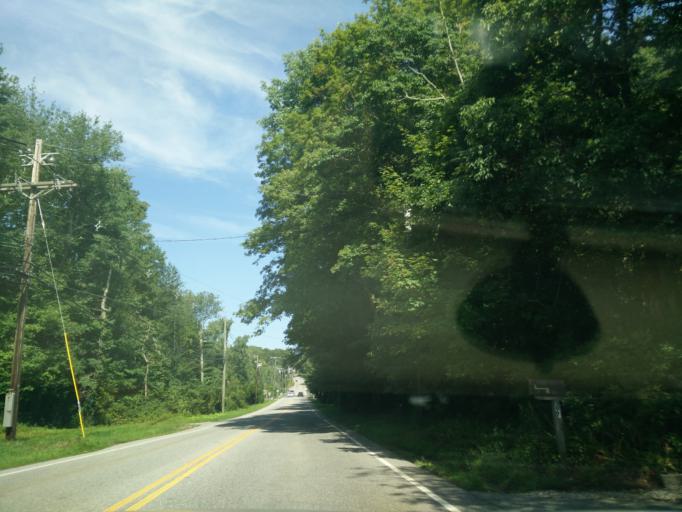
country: US
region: Connecticut
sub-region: Middlesex County
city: Clinton
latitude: 41.3521
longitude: -72.5619
